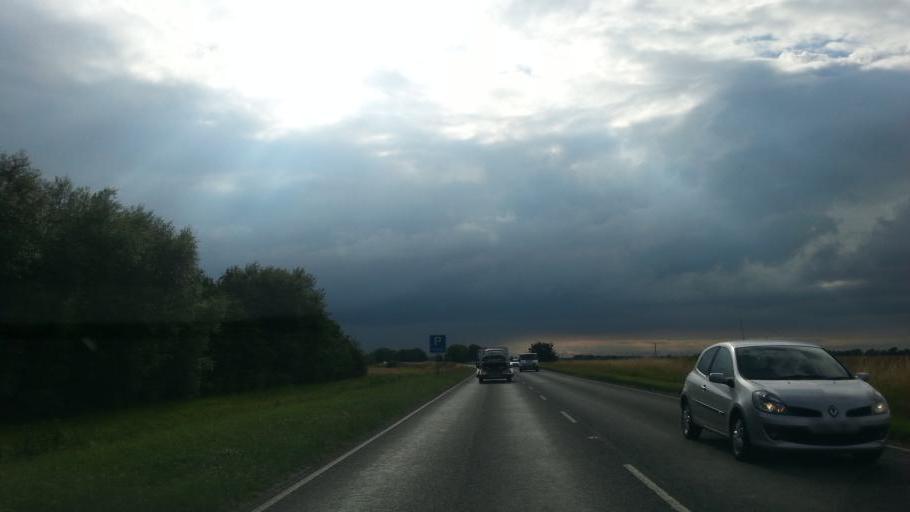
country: GB
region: England
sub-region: Lincolnshire
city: Heckington
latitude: 52.9845
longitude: -0.2374
